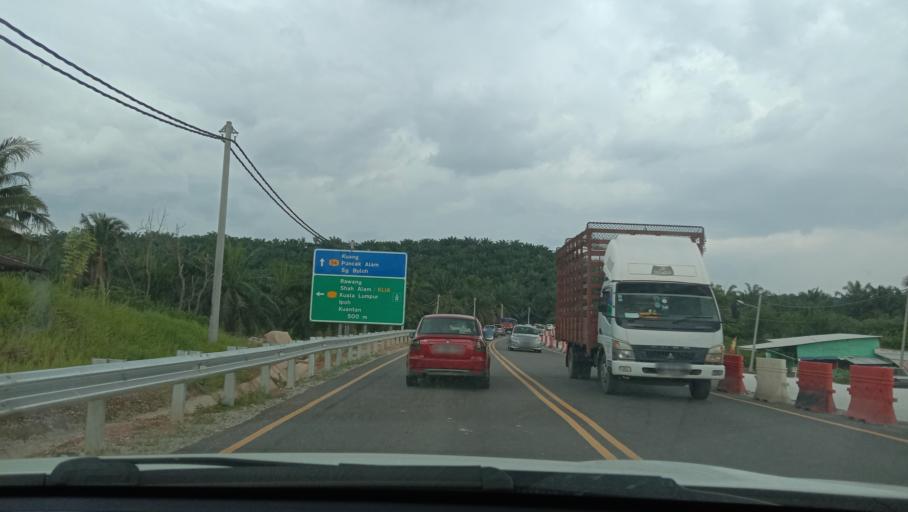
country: MY
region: Selangor
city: Batu Arang
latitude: 3.2626
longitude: 101.4607
